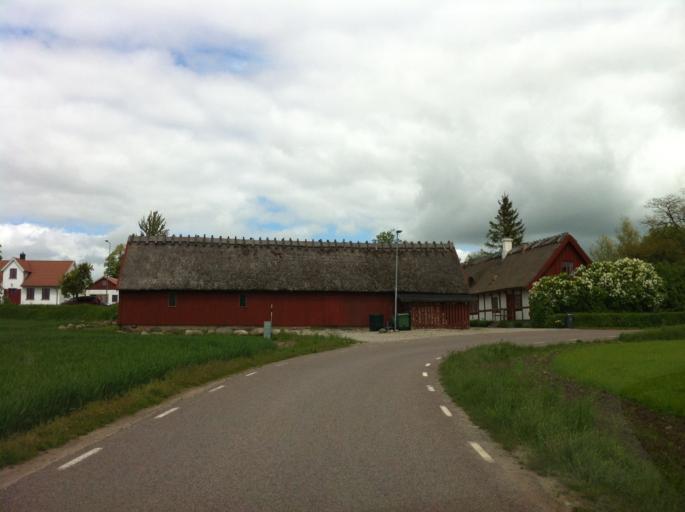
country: SE
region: Skane
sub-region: Svalovs Kommun
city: Teckomatorp
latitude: 55.8219
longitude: 13.0651
